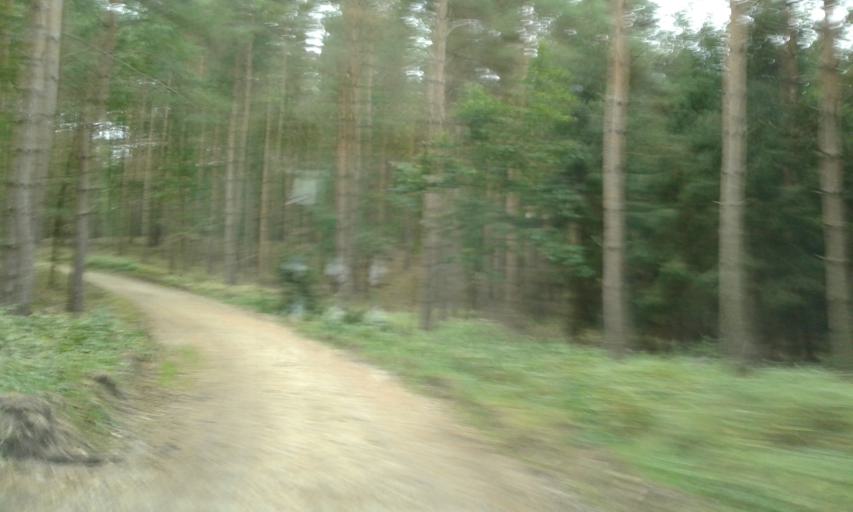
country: PL
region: West Pomeranian Voivodeship
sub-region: Powiat choszczenski
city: Pelczyce
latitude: 53.0911
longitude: 15.2409
